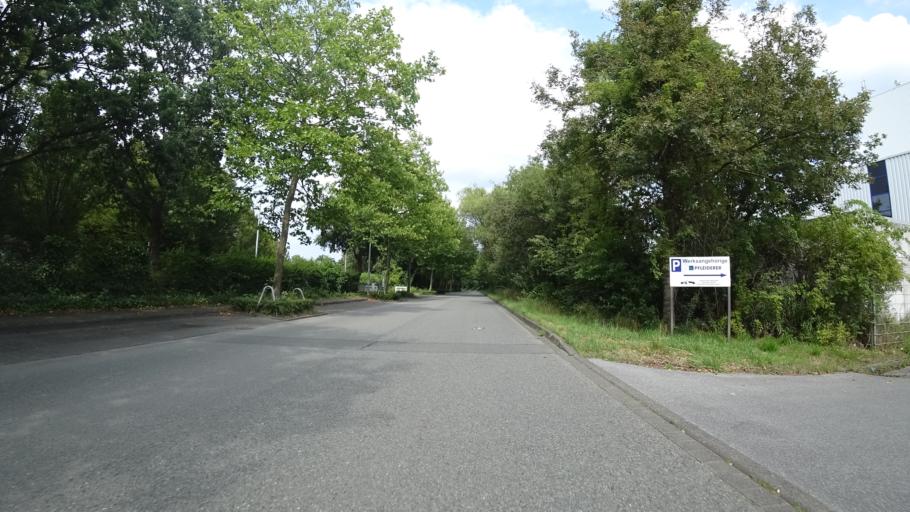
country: DE
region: North Rhine-Westphalia
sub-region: Regierungsbezirk Detmold
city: Guetersloh
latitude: 51.9271
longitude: 8.4101
